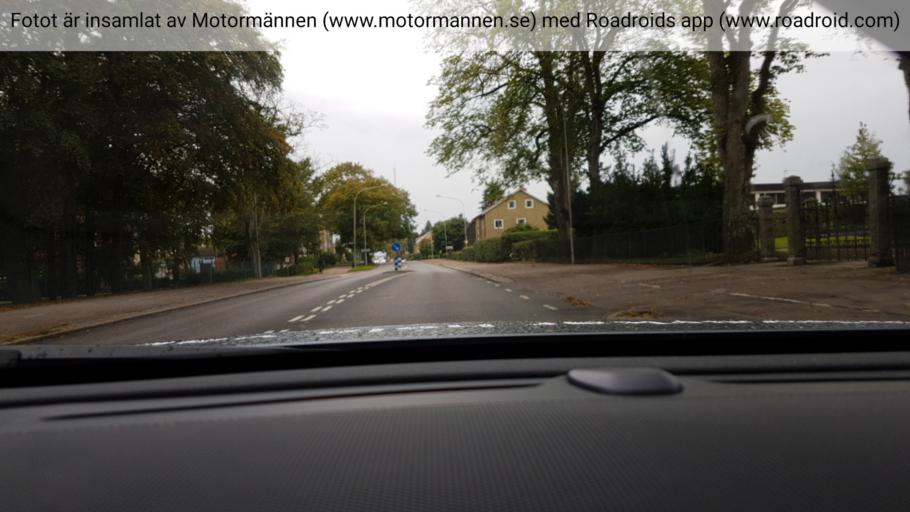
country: SE
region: Vaestra Goetaland
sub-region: Vanersborgs Kommun
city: Vanersborg
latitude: 58.3742
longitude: 12.3209
